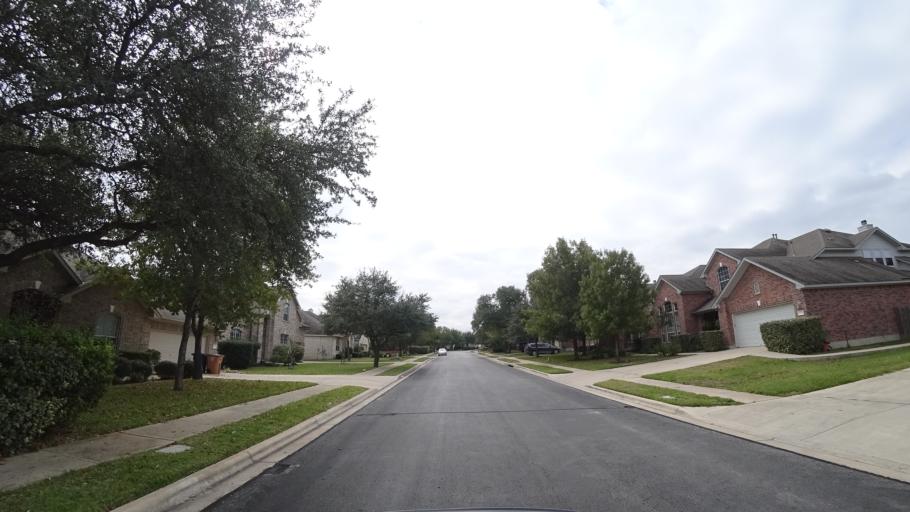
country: US
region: Texas
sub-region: Travis County
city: Shady Hollow
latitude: 30.1905
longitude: -97.8995
